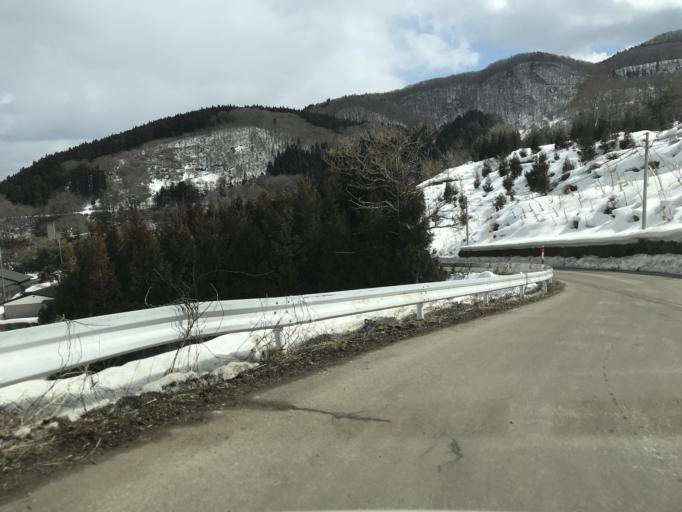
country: JP
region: Miyagi
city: Furukawa
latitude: 38.7286
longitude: 140.7624
